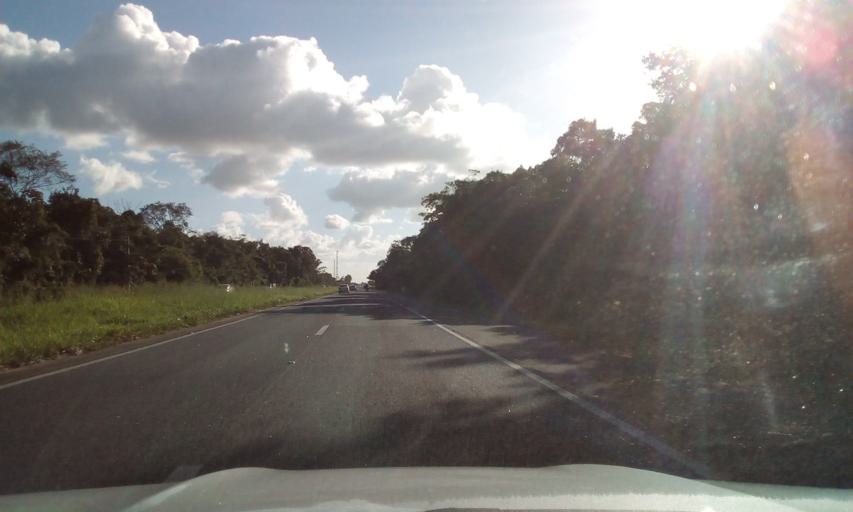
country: BR
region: Paraiba
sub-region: Cruz Do Espirito Santo
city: Cruz do Espirito Santo
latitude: -7.2018
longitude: -35.0998
